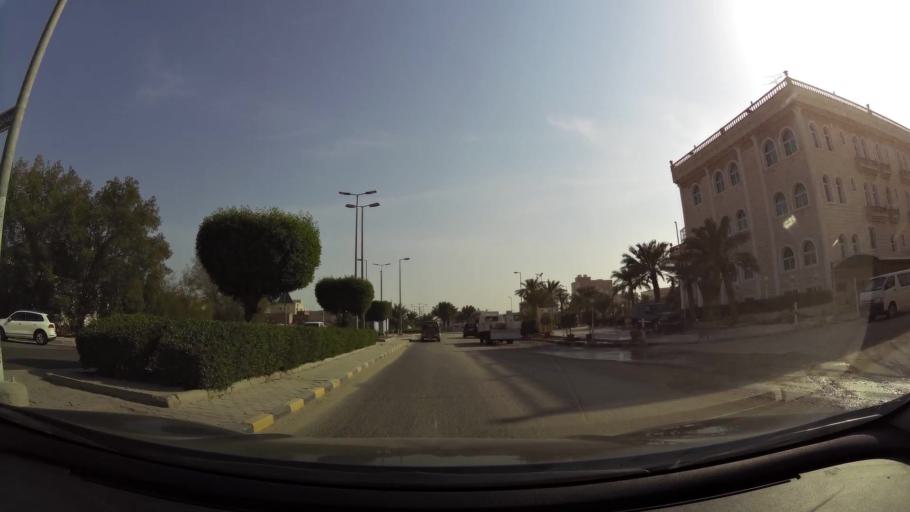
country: KW
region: Al Ahmadi
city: Ar Riqqah
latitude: 29.1446
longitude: 48.1068
